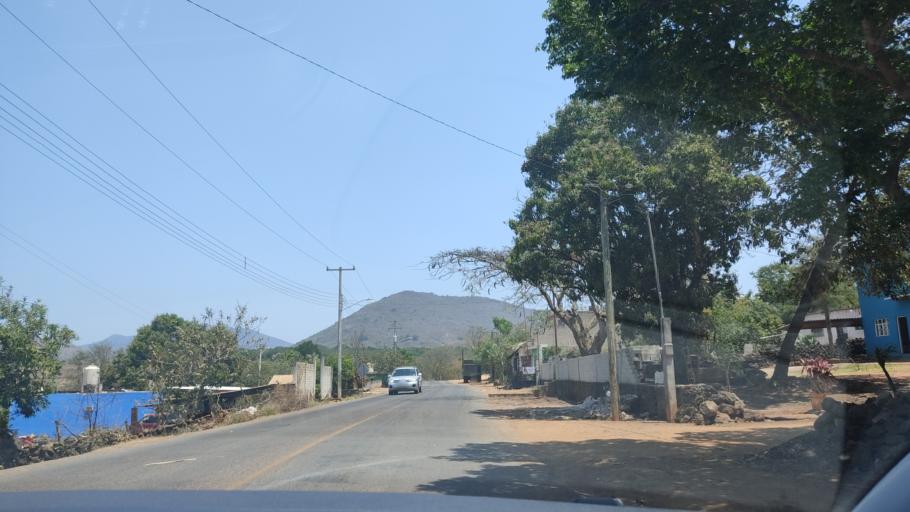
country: MX
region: Nayarit
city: Puga
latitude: 21.5770
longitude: -104.7828
